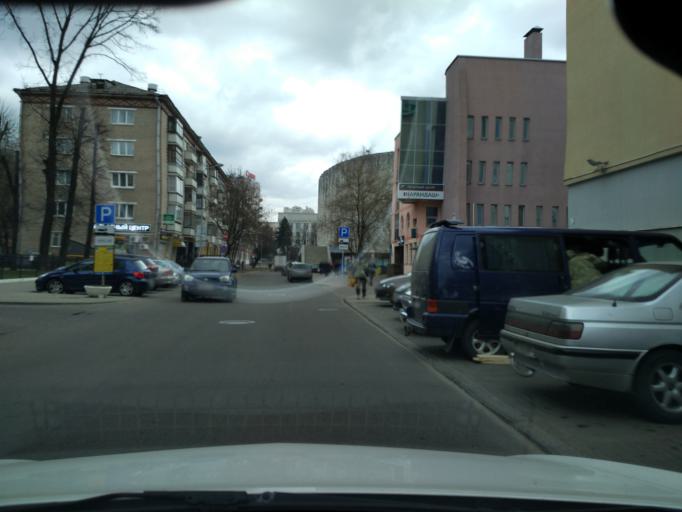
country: BY
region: Minsk
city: Minsk
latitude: 53.9234
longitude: 27.5958
